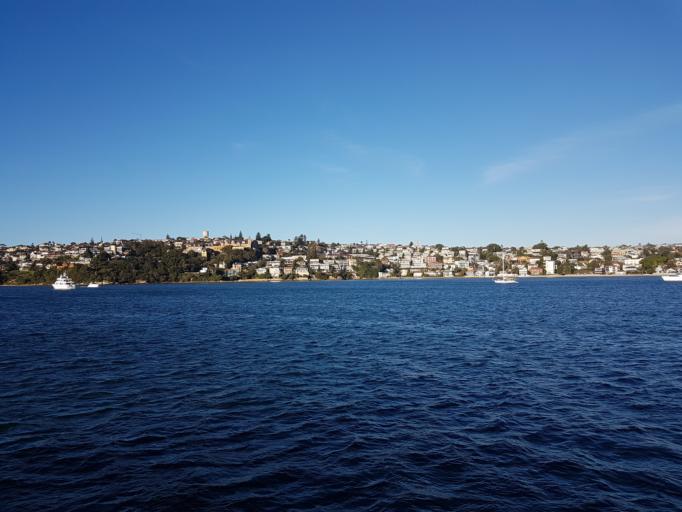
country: AU
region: New South Wales
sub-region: Woollahra
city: Point Piper
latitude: -33.8658
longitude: 151.2612
